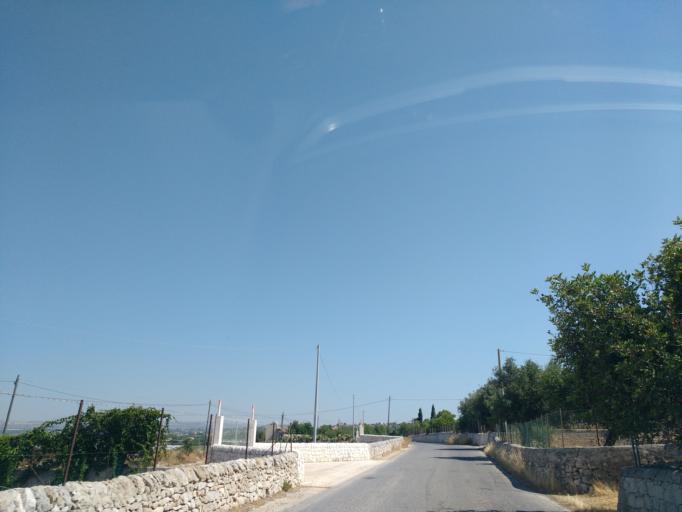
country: IT
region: Sicily
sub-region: Ragusa
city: Cava d'Aliga
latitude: 36.7574
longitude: 14.7032
